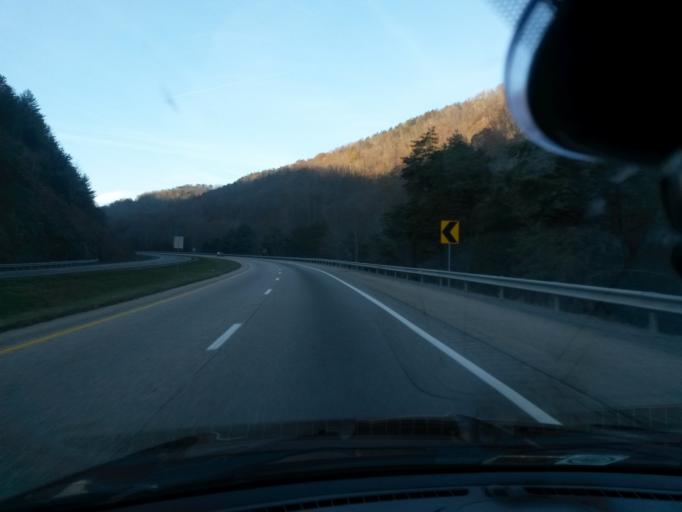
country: US
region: West Virginia
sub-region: Greenbrier County
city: White Sulphur Springs
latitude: 37.8239
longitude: -80.1680
